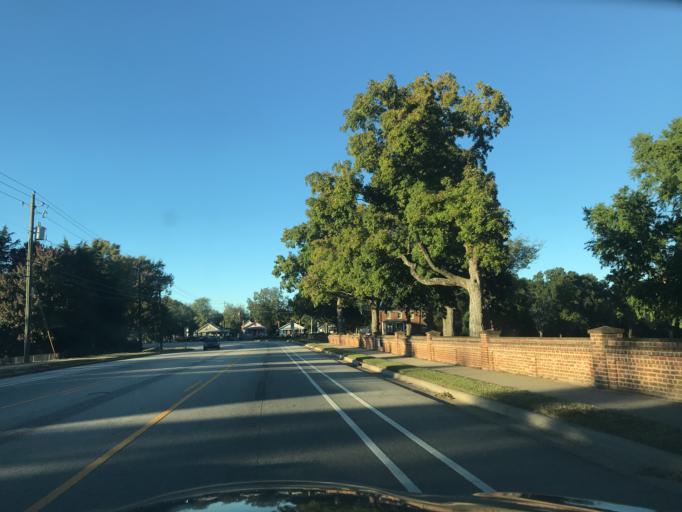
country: US
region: North Carolina
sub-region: Wake County
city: Raleigh
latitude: 35.7732
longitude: -78.6214
